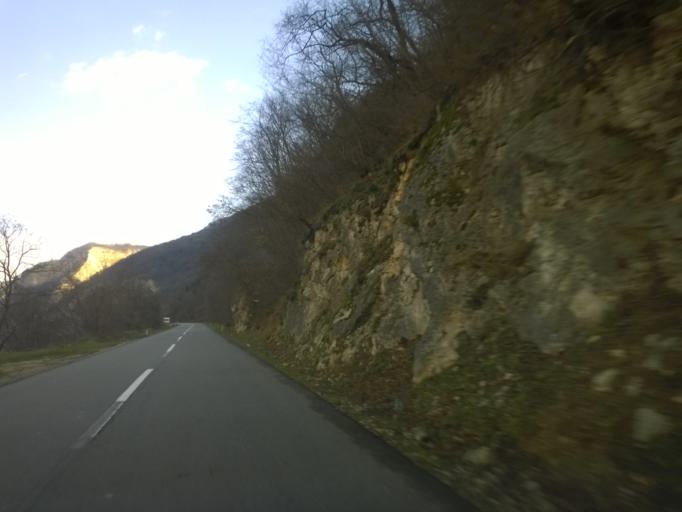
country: RO
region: Caras-Severin
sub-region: Comuna Pescari
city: Coronini
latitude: 44.6529
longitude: 21.7143
